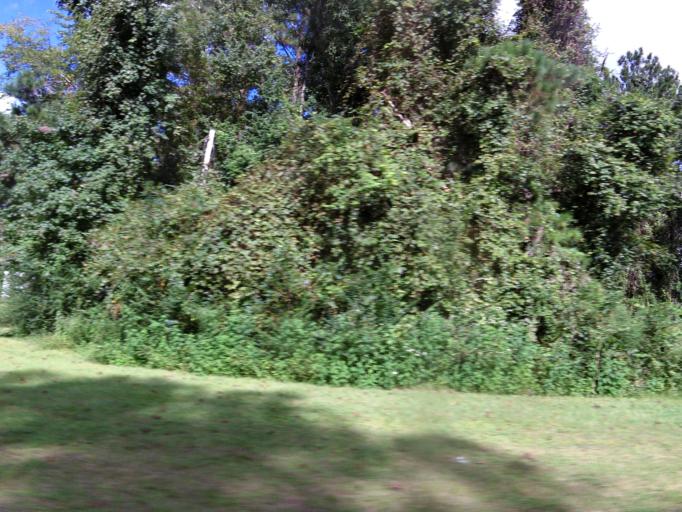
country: US
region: Georgia
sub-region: Camden County
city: Kingsland
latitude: 30.8342
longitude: -81.6970
